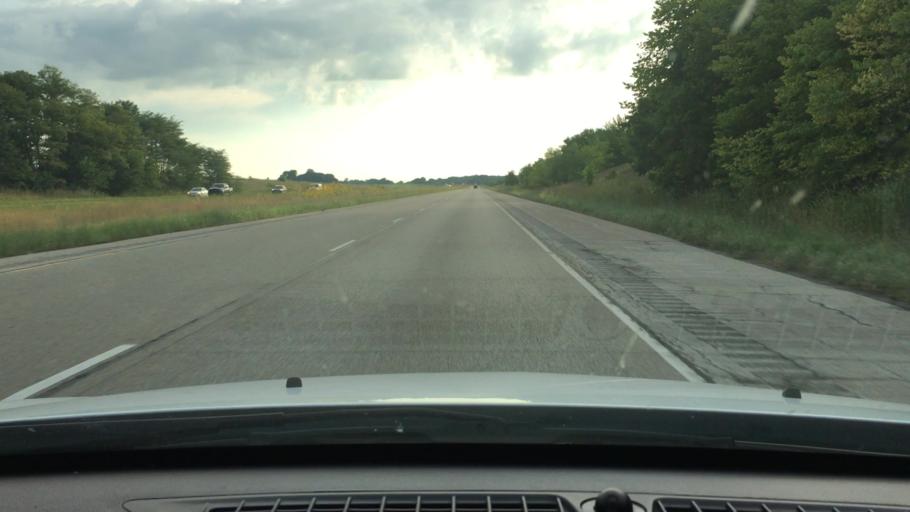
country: US
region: Illinois
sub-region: McLean County
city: Twin Grove
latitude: 40.3534
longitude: -89.1150
